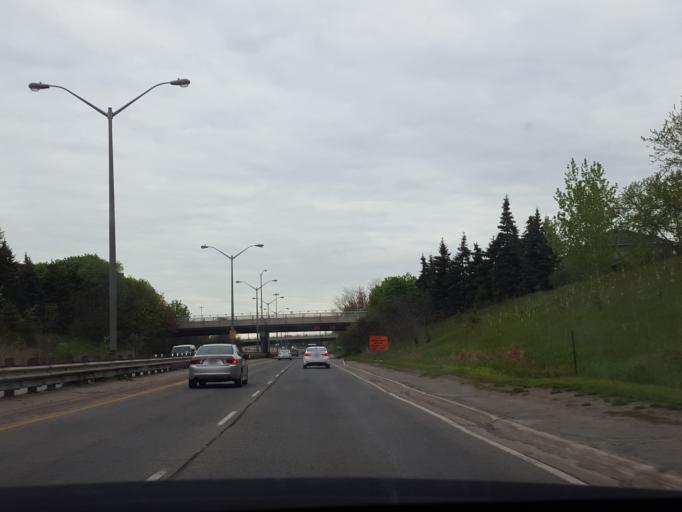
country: CA
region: Ontario
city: Toronto
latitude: 43.7078
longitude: -79.4977
